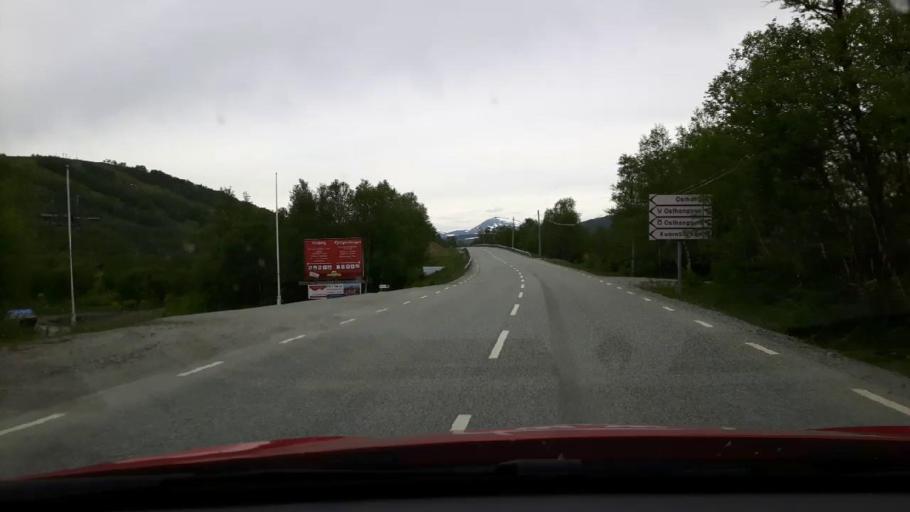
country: NO
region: Sor-Trondelag
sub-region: Tydal
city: Aas
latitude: 62.6967
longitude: 12.3991
